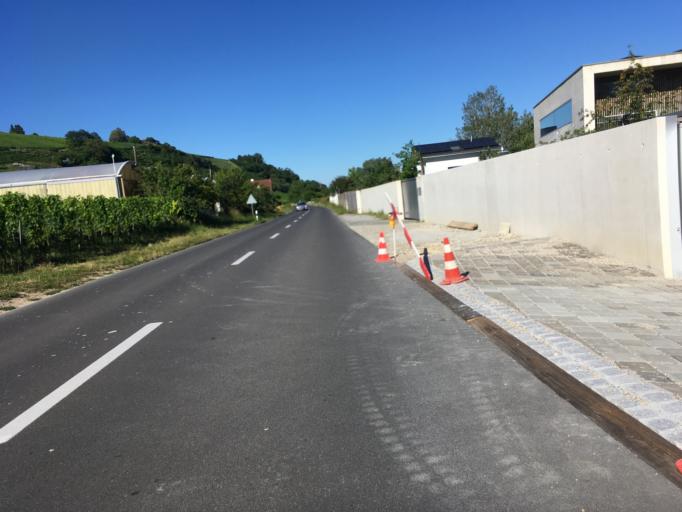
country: CH
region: Fribourg
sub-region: See District
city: Bas-Vully
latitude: 46.9439
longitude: 7.0713
